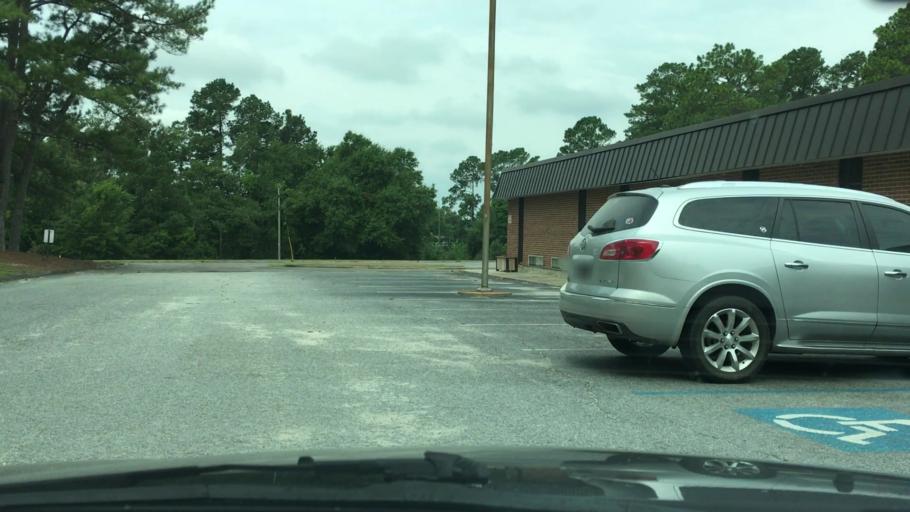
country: US
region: South Carolina
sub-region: Aiken County
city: Graniteville
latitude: 33.5614
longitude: -81.8028
